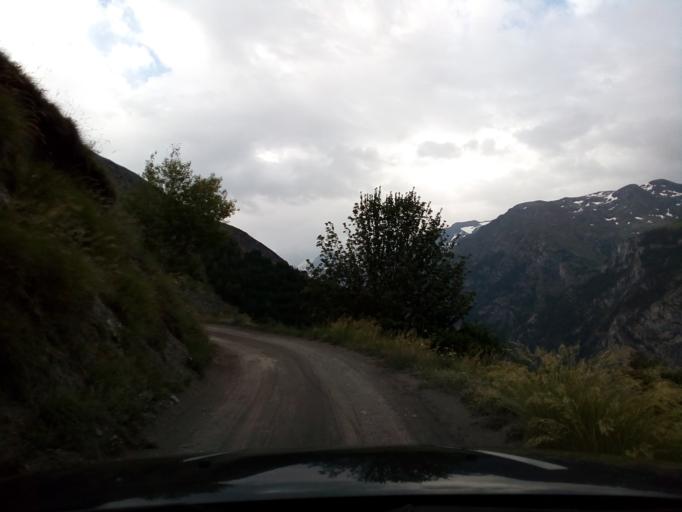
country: FR
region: Rhone-Alpes
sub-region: Departement de l'Isere
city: Mont-de-Lans
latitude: 45.0519
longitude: 6.1556
